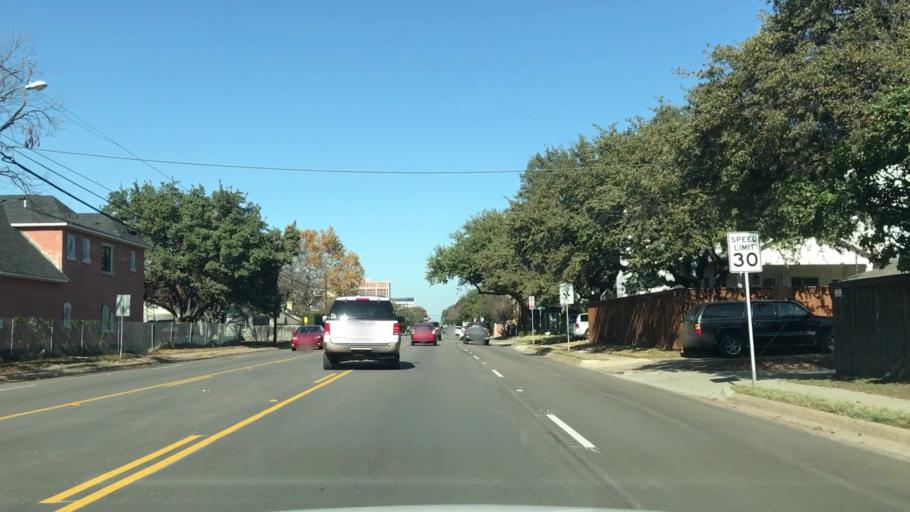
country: US
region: Texas
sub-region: Dallas County
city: University Park
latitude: 32.8541
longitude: -96.8042
